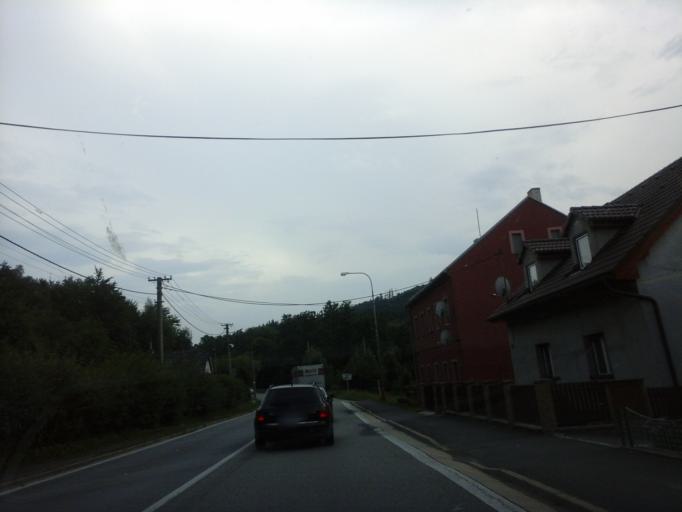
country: CZ
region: Pardubicky
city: Brnenec
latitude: 49.6174
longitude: 16.5310
